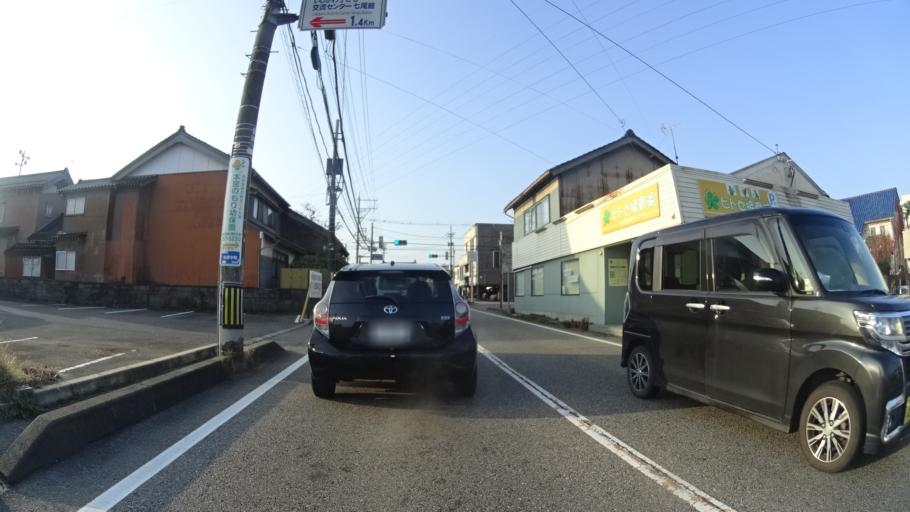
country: JP
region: Ishikawa
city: Nanao
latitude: 37.0336
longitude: 136.9680
